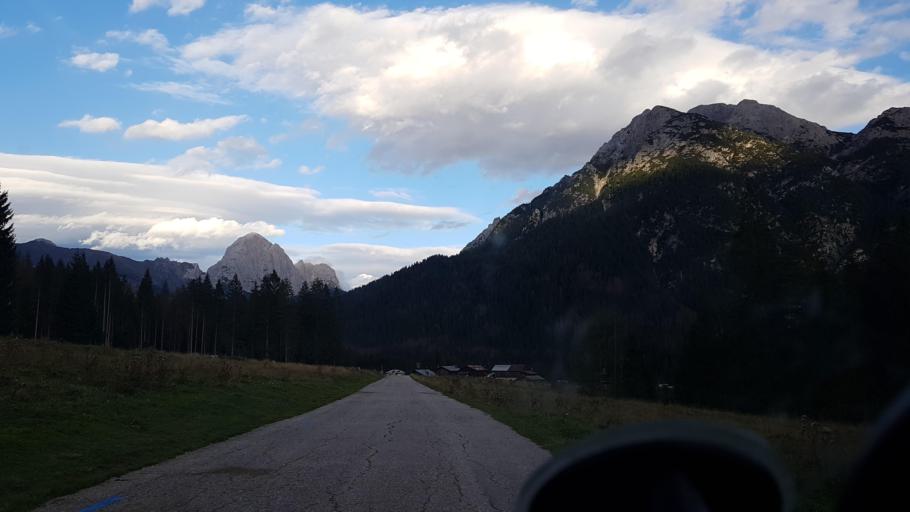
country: IT
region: Veneto
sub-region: Provincia di Belluno
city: San Pietro di Cadore
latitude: 46.6102
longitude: 12.6169
